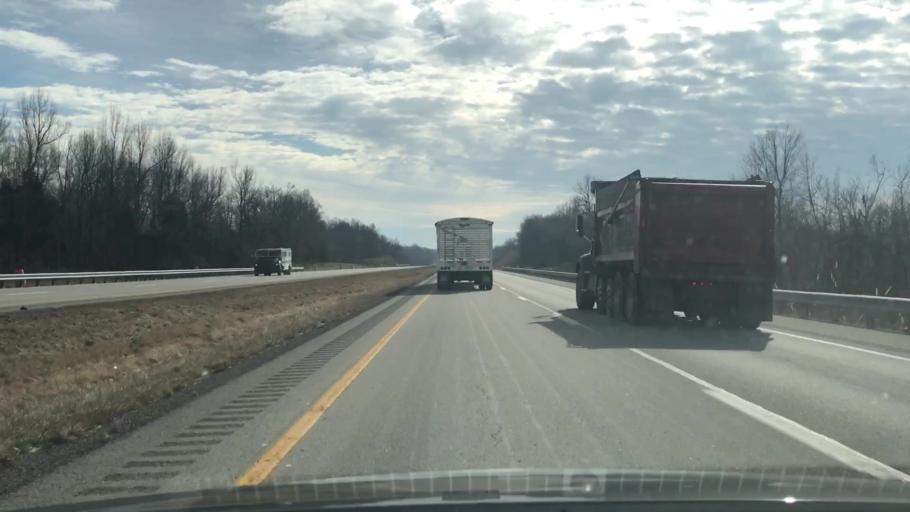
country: US
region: Kentucky
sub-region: Daviess County
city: Masonville
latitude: 37.5828
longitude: -86.9590
